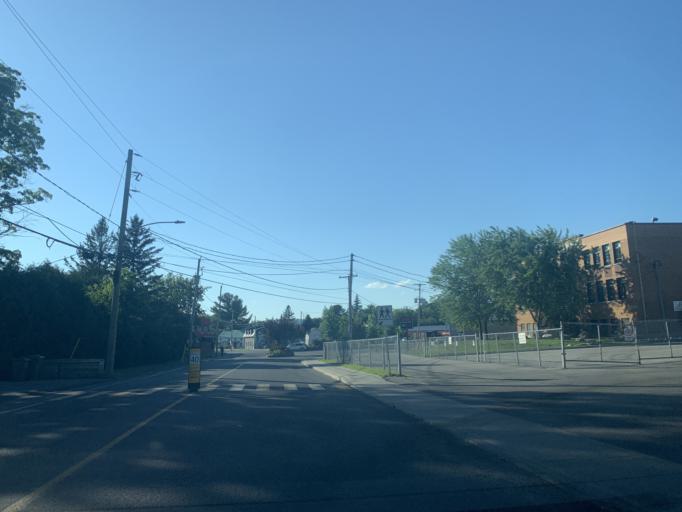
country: CA
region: Ontario
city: Hawkesbury
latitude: 45.6258
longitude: -74.6036
